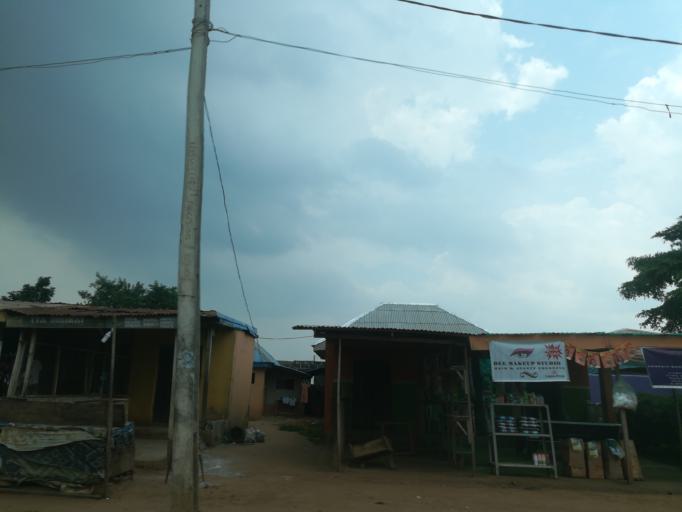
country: NG
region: Lagos
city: Ikorodu
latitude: 6.5991
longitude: 3.5883
